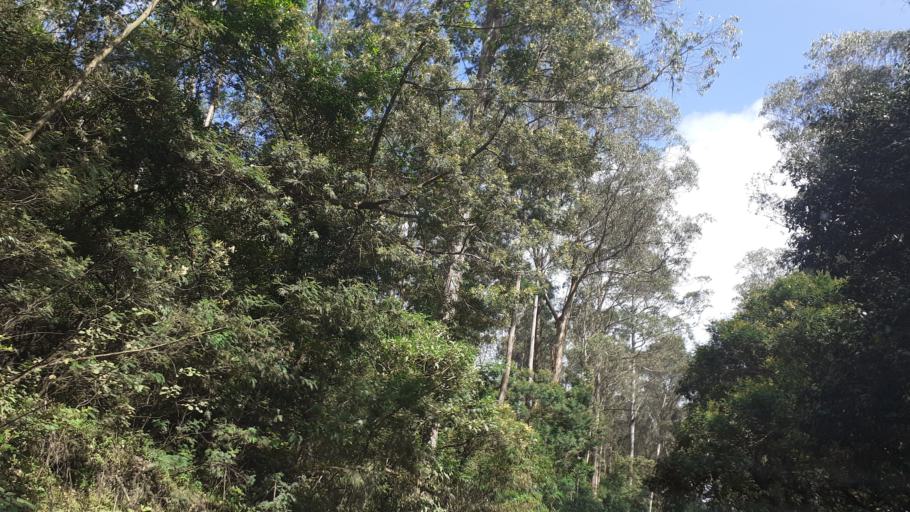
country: IN
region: Tamil Nadu
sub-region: Dindigul
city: Kodaikanal
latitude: 10.2303
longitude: 77.4238
